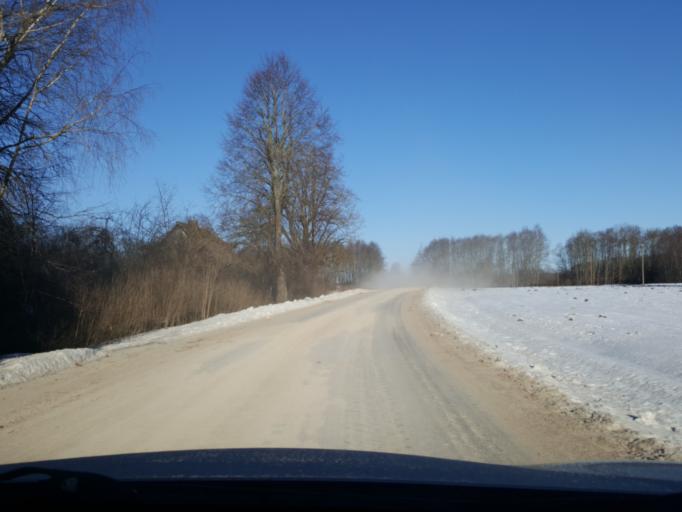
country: EE
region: Viljandimaa
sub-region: Viljandi linn
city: Viljandi
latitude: 58.4259
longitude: 25.5323
